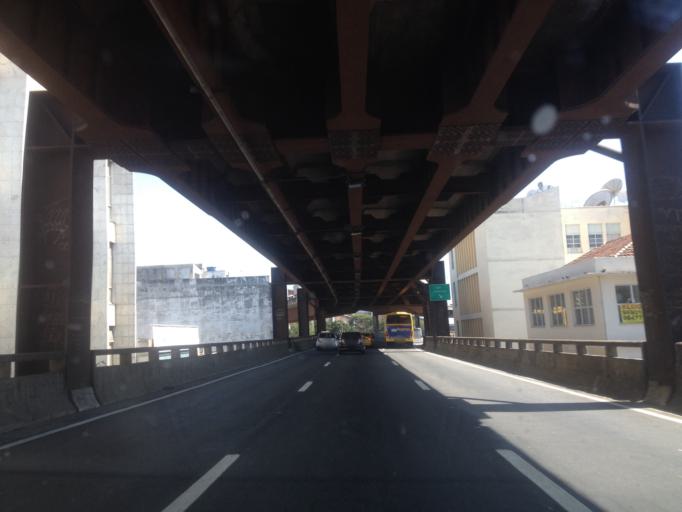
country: BR
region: Rio de Janeiro
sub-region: Rio De Janeiro
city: Rio de Janeiro
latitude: -22.8994
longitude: -43.2182
